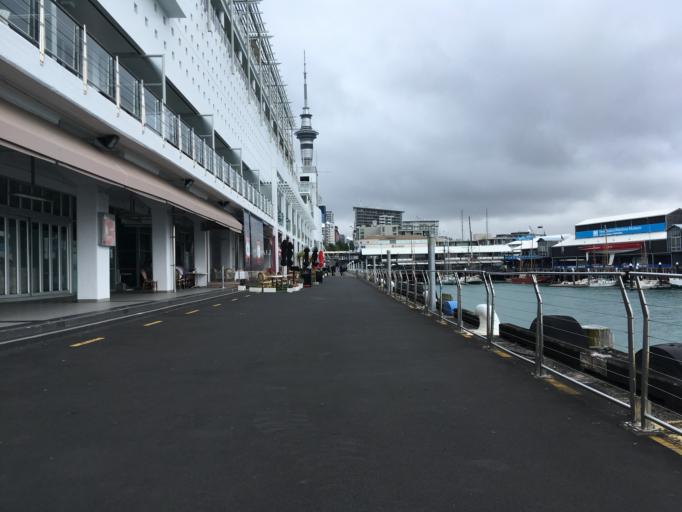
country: NZ
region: Auckland
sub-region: Auckland
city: Auckland
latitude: -36.8403
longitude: 174.7649
